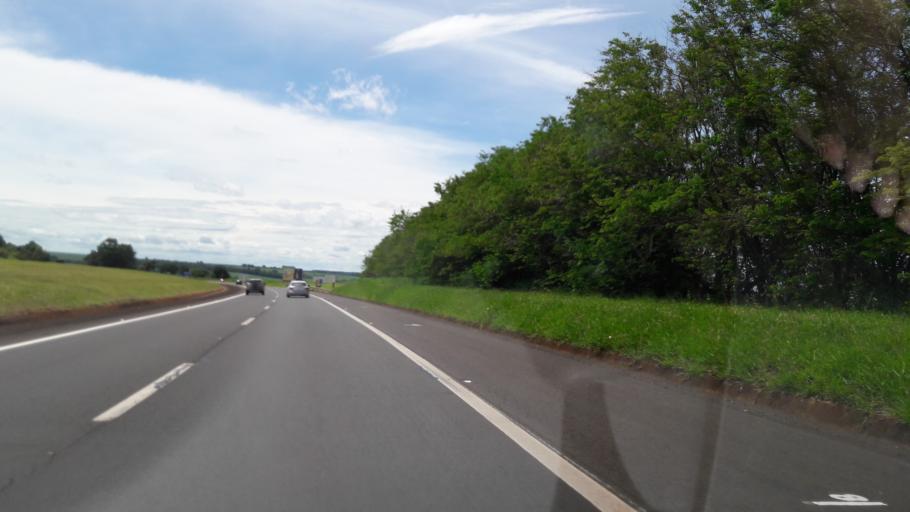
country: BR
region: Sao Paulo
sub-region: Avare
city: Avare
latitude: -22.9559
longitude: -48.8204
